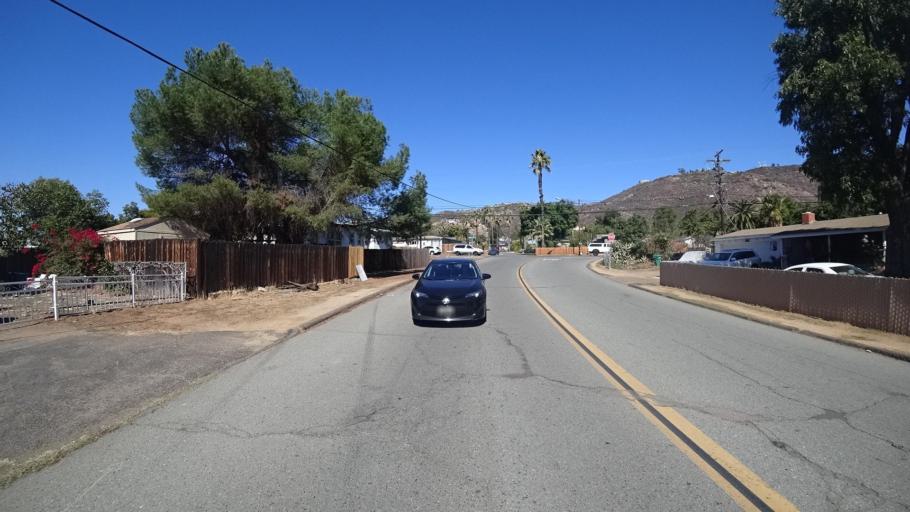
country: US
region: California
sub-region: San Diego County
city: Winter Gardens
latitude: 32.8231
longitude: -116.9498
